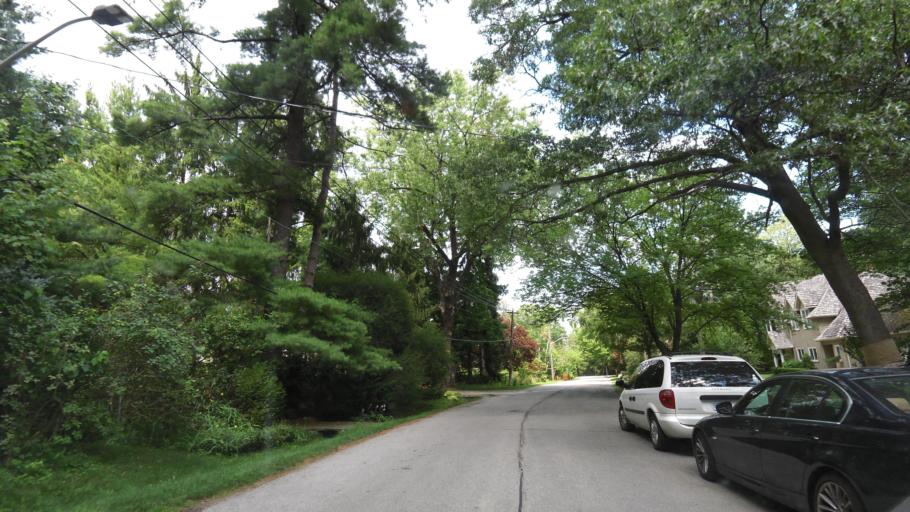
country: CA
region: Ontario
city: Mississauga
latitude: 43.5614
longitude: -79.5986
